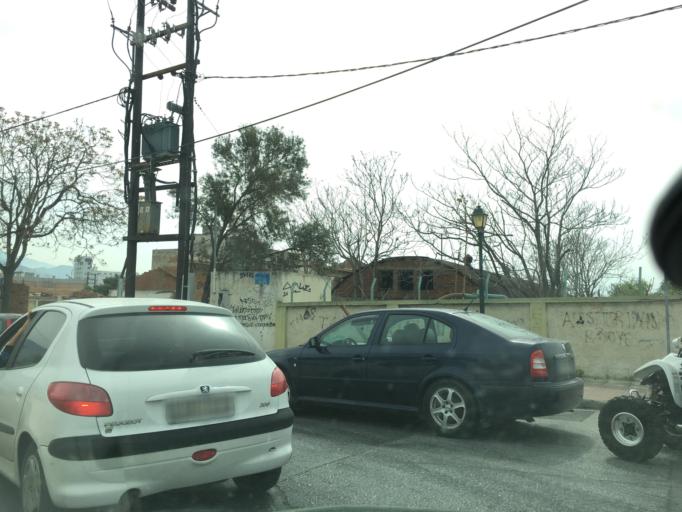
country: GR
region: Thessaly
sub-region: Nomos Magnisias
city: Nea Ionia
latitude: 39.3606
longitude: 22.9329
